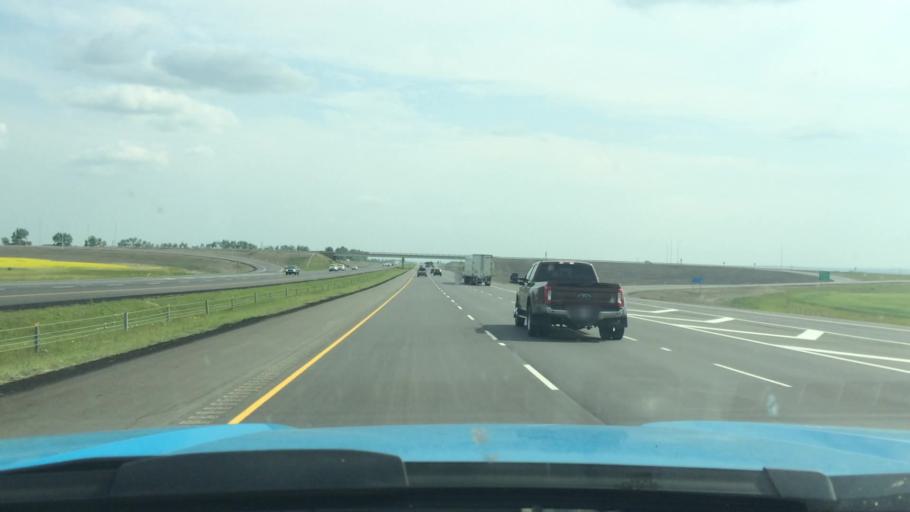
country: CA
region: Alberta
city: Crossfield
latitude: 51.3916
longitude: -114.0020
